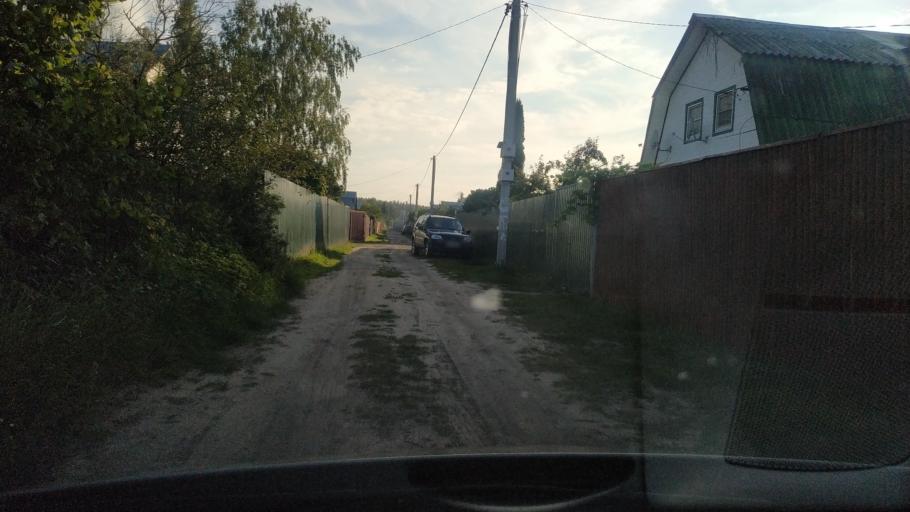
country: RU
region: Moskovskaya
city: Roshal'
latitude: 55.6446
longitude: 39.7945
